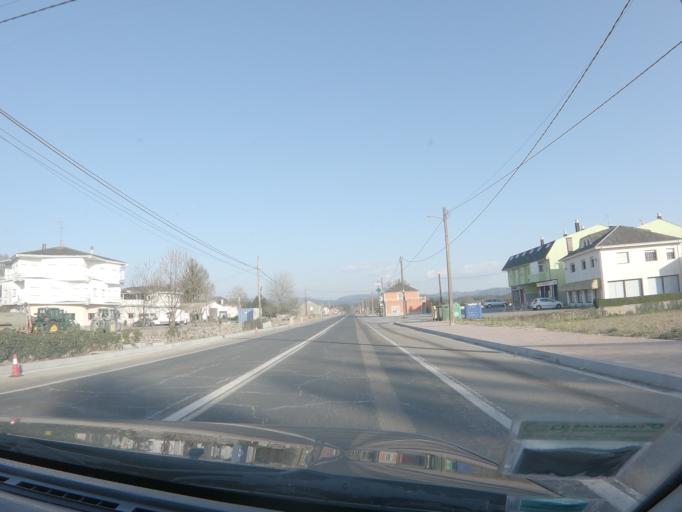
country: ES
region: Galicia
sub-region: Provincia de Lugo
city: Corgo
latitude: 42.9438
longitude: -7.4334
